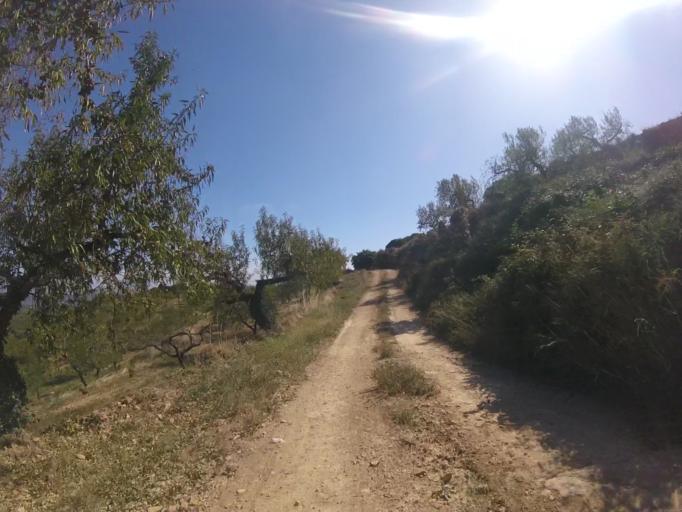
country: ES
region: Valencia
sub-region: Provincia de Castello
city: Sierra-Engarceran
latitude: 40.2723
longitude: 0.0059
